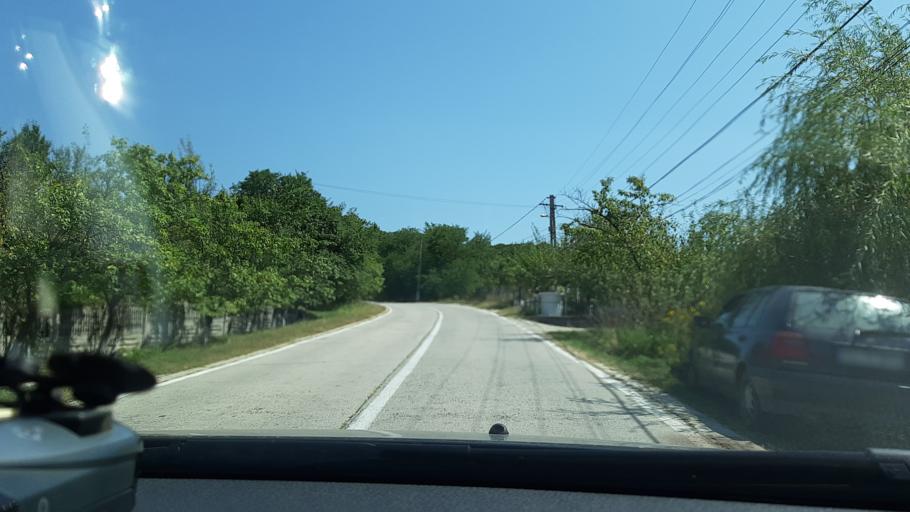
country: RO
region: Gorj
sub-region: Comuna Logresti-Mosteni
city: Logresti Mosteni
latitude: 44.9088
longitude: 23.7544
